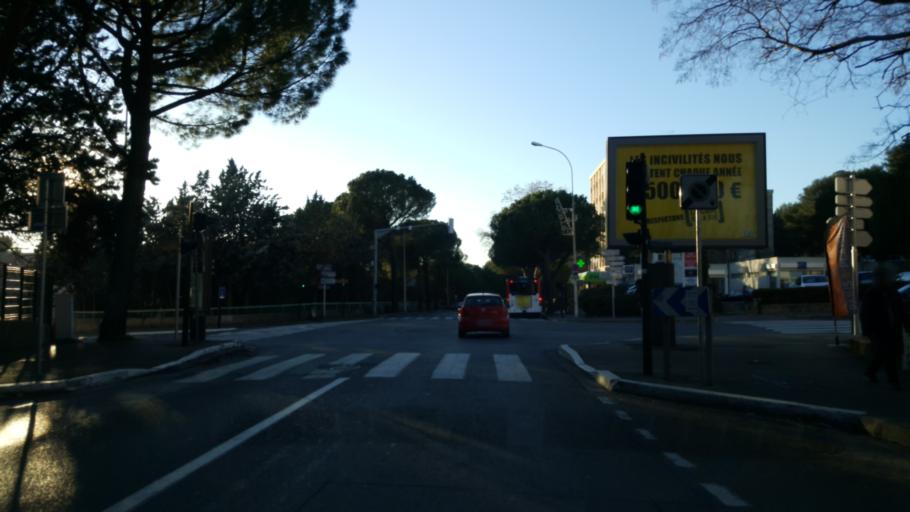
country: FR
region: Provence-Alpes-Cote d'Azur
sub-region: Departement des Bouches-du-Rhone
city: Aix-en-Provence
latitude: 43.5141
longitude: 5.4619
